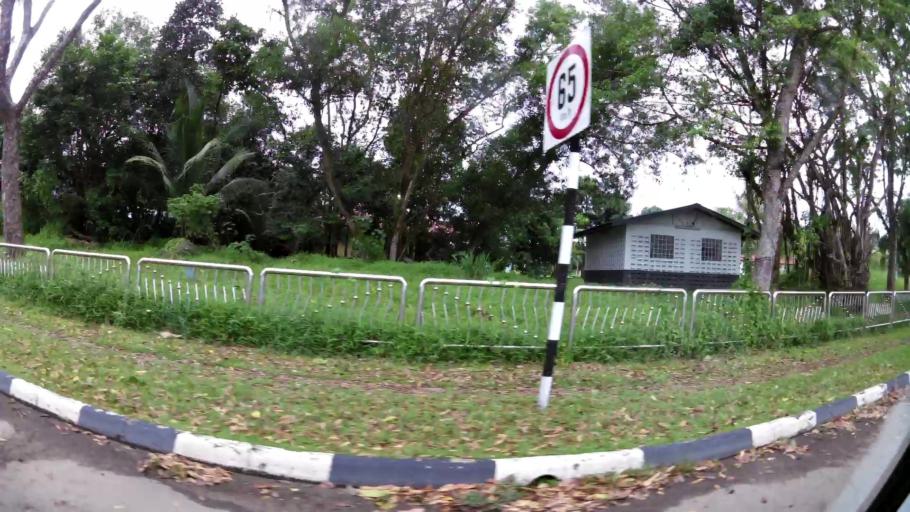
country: BN
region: Brunei and Muara
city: Bandar Seri Begawan
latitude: 4.8993
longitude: 114.9275
